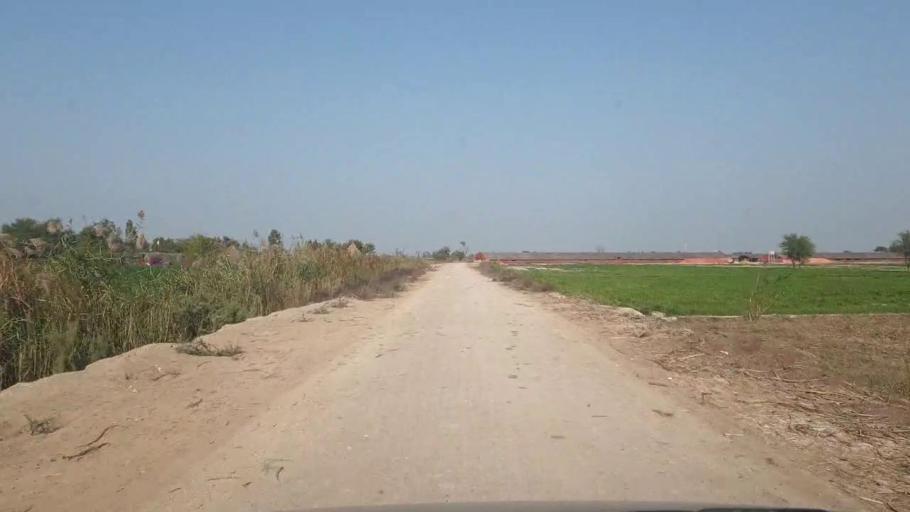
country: PK
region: Sindh
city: Bhit Shah
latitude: 25.8213
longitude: 68.5738
